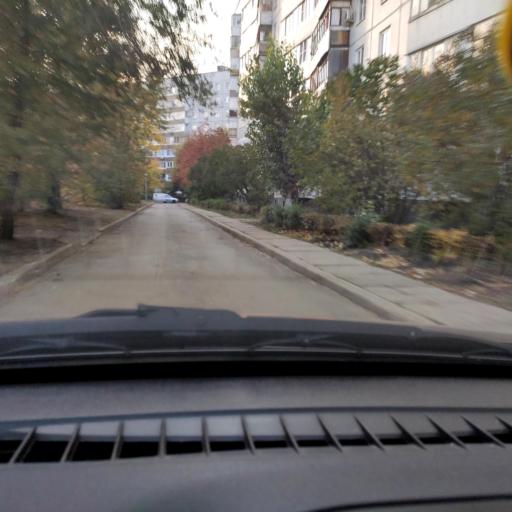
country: RU
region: Samara
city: Tol'yatti
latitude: 53.5033
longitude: 49.2840
